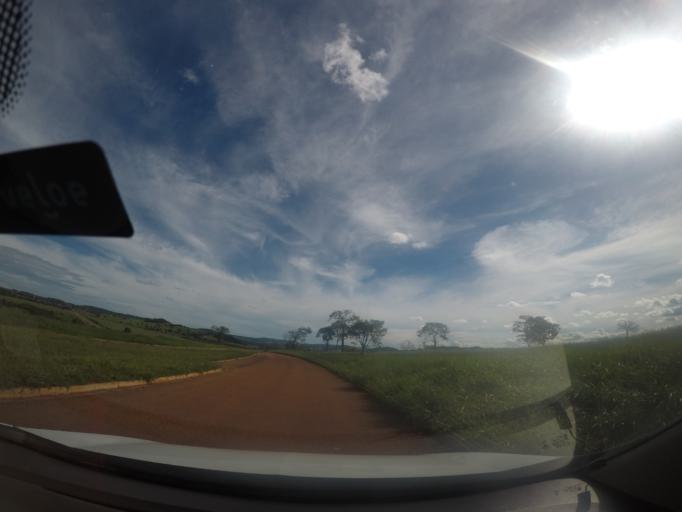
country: BR
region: Goias
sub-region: Inhumas
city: Inhumas
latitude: -16.4086
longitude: -49.4723
